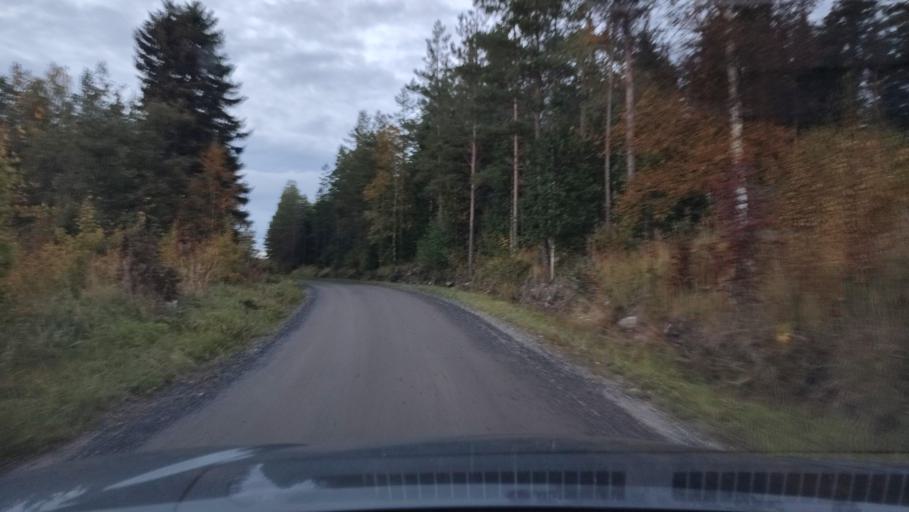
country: FI
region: Ostrobothnia
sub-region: Sydosterbotten
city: Kristinestad
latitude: 62.2764
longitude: 21.5158
